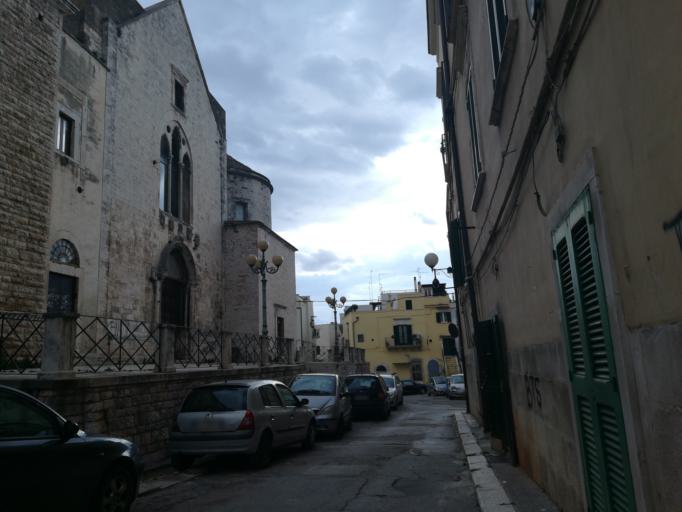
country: IT
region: Apulia
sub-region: Provincia di Bari
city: Bitonto
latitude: 41.1057
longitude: 16.6914
